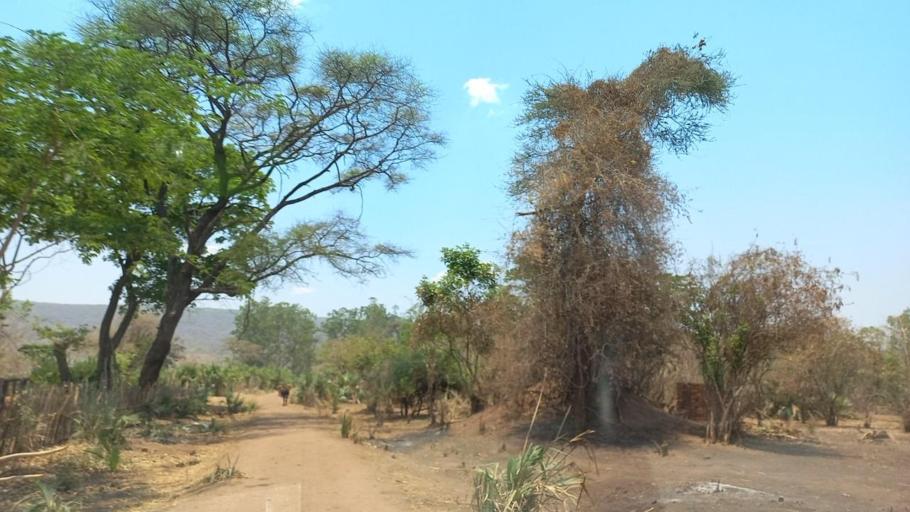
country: ZM
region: Lusaka
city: Luangwa
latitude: -15.1969
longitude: 30.1737
